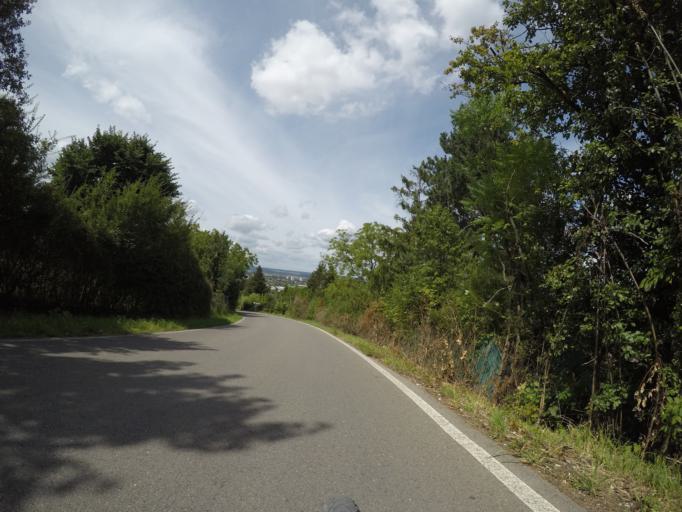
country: DE
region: Baden-Wuerttemberg
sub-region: Tuebingen Region
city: Eningen unter Achalm
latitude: 48.4984
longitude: 9.2345
